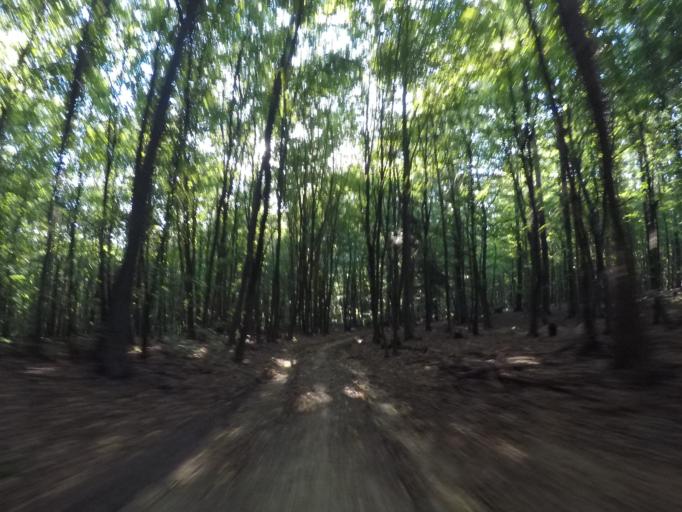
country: SK
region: Kosicky
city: Kosice
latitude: 48.7307
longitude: 21.1555
